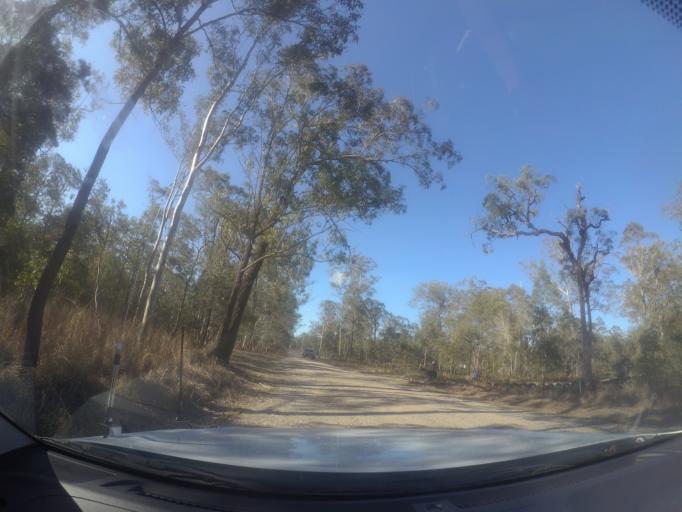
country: AU
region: Queensland
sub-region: Logan
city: Park Ridge South
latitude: -27.7349
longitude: 153.0539
